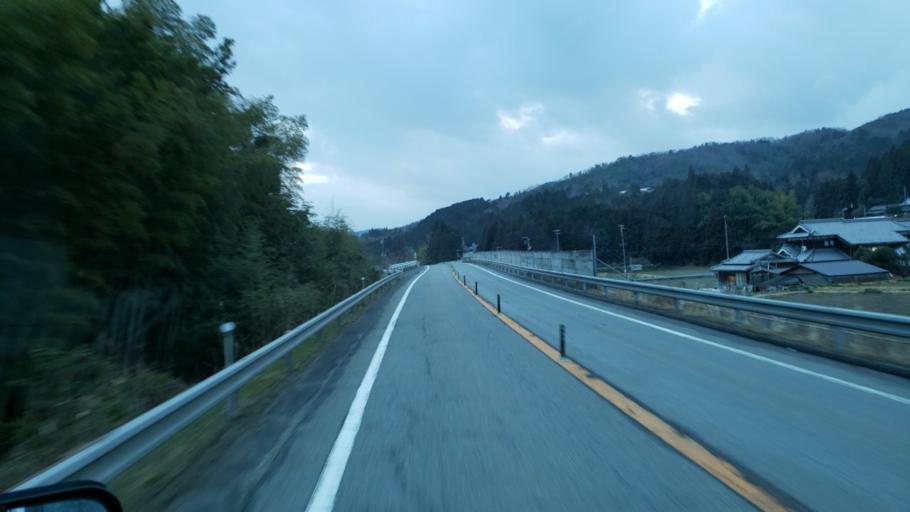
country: JP
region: Hyogo
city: Nishiwaki
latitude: 35.0849
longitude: 134.7764
